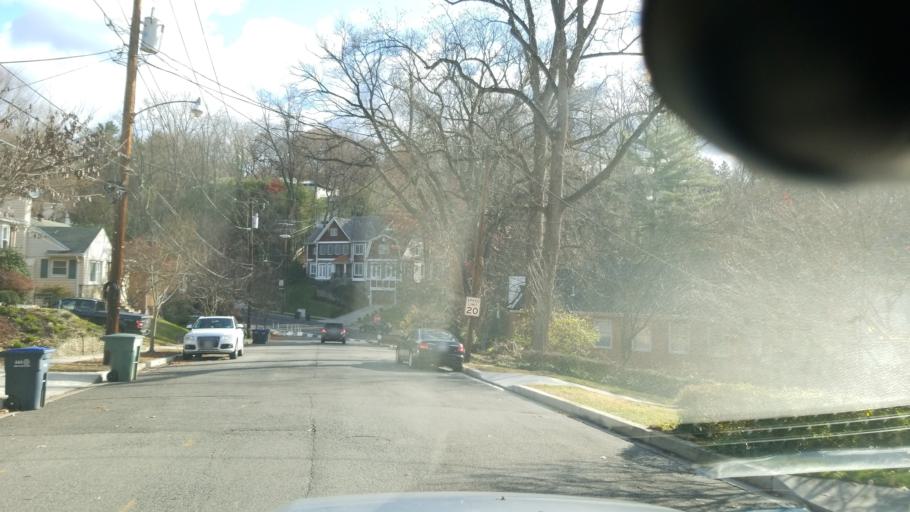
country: US
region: Maryland
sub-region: Montgomery County
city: Brookmont
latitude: 38.9303
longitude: -77.1008
